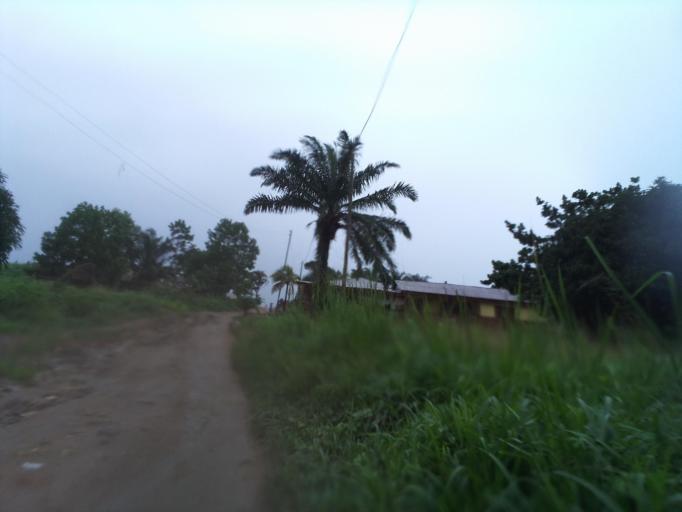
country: SL
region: Eastern Province
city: Kenema
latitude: 7.8547
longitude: -11.1904
